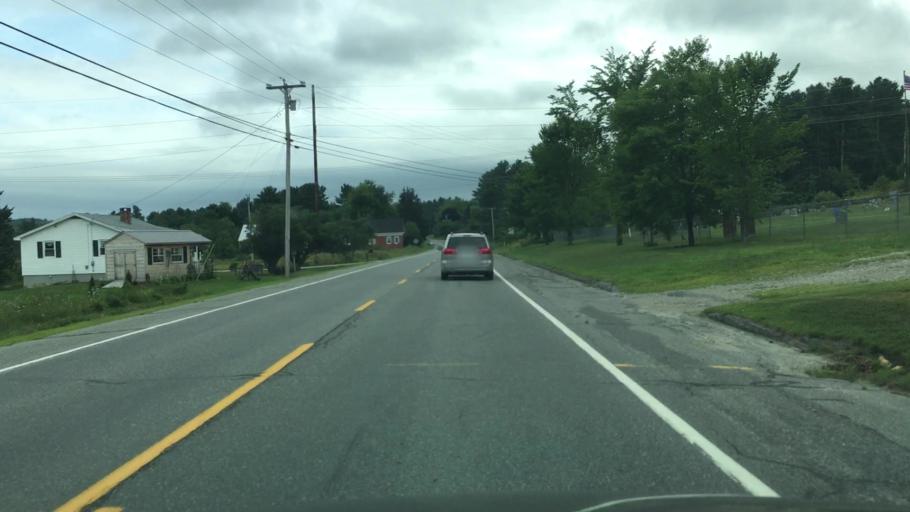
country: US
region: Maine
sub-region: Waldo County
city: Frankfort
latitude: 44.5510
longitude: -68.8643
